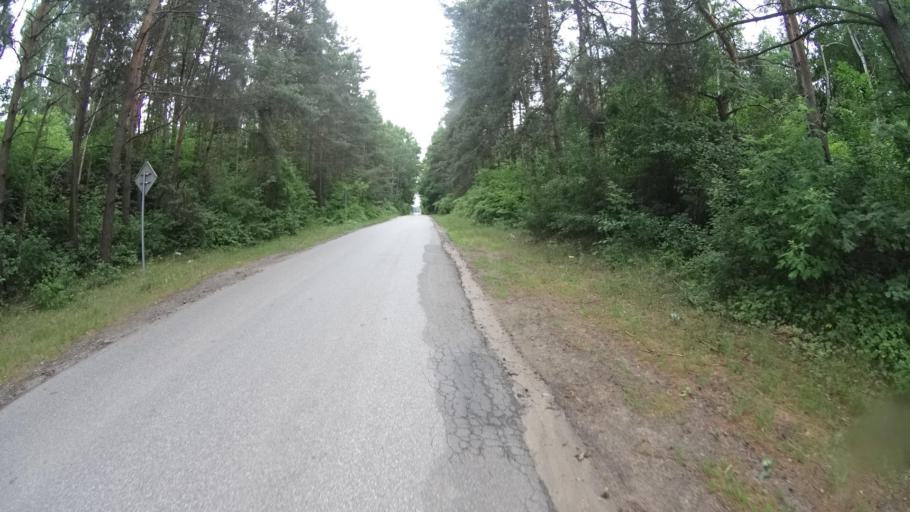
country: PL
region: Masovian Voivodeship
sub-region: Powiat grojecki
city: Belsk Duzy
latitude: 51.7995
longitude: 20.8593
